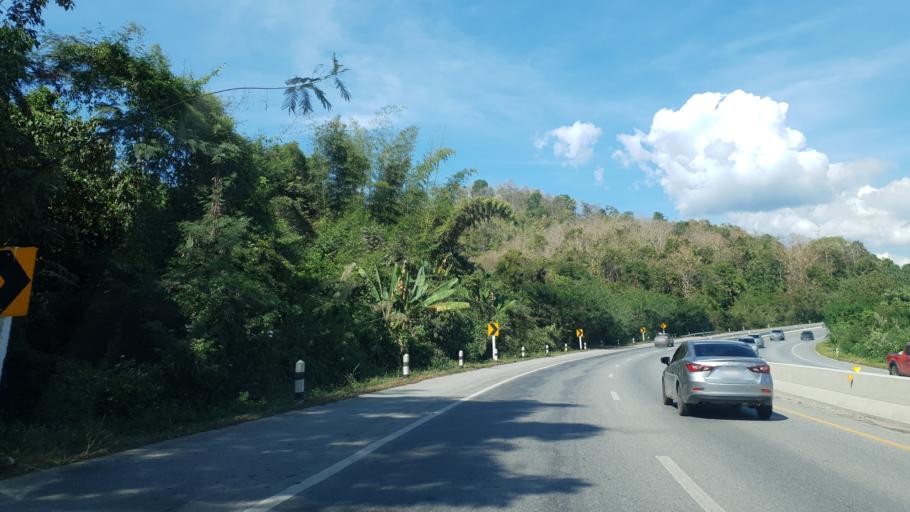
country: TH
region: Uttaradit
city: Uttaradit
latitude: 17.7623
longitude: 100.1316
